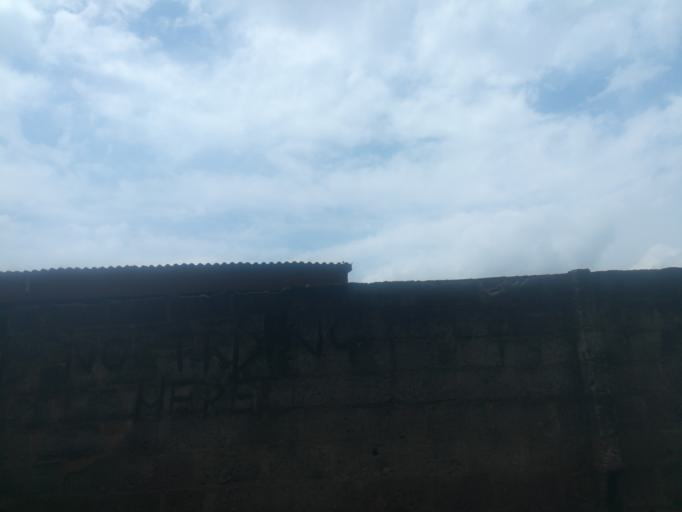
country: NG
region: Lagos
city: Ojota
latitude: 6.5903
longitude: 3.3876
